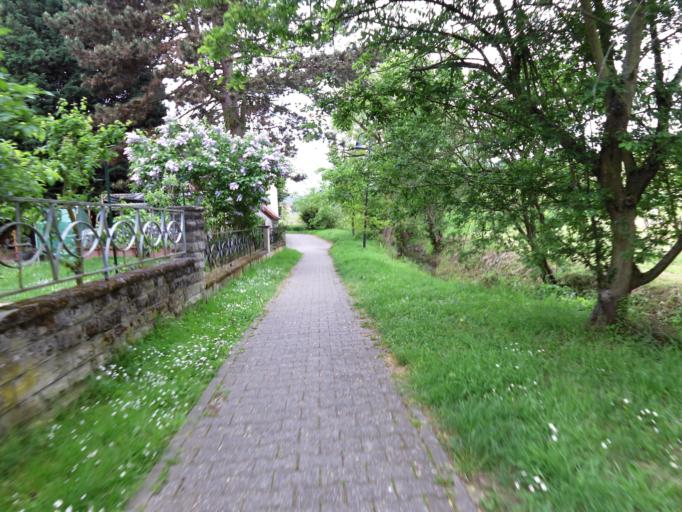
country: DE
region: Rheinland-Pfalz
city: Kleinkarlbach
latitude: 49.5414
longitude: 8.1602
